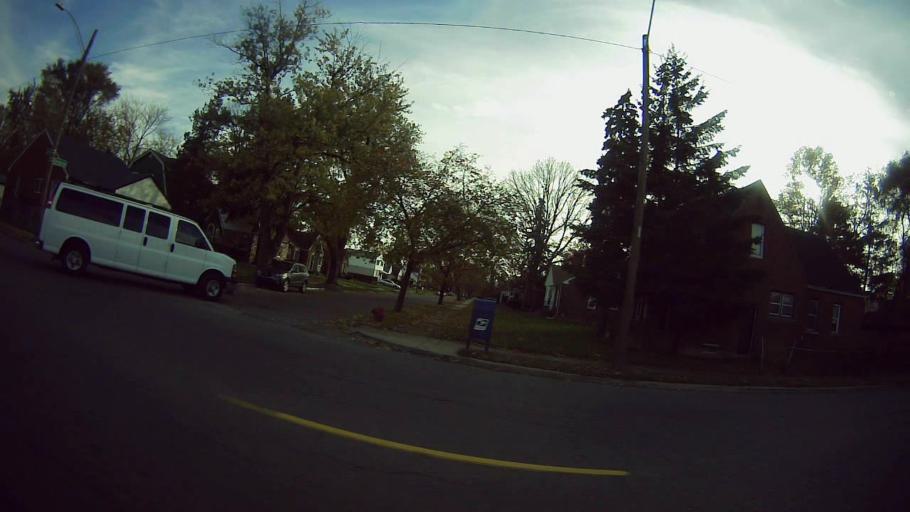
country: US
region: Michigan
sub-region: Oakland County
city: Oak Park
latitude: 42.4085
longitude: -83.2098
